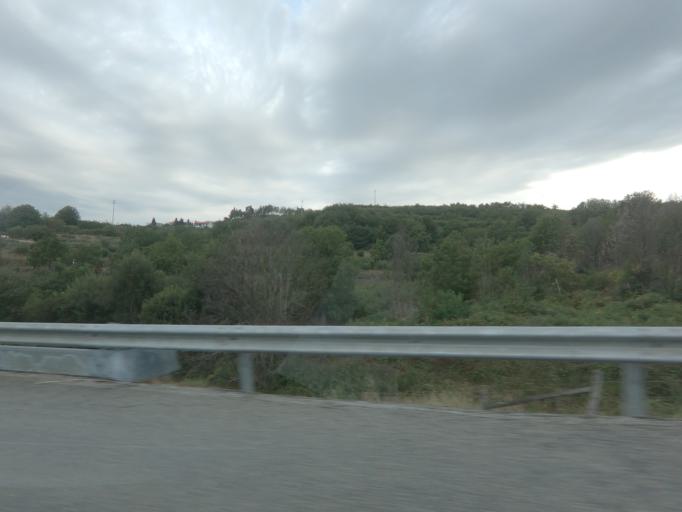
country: PT
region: Viseu
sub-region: Lamego
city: Lamego
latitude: 41.0737
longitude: -7.8136
